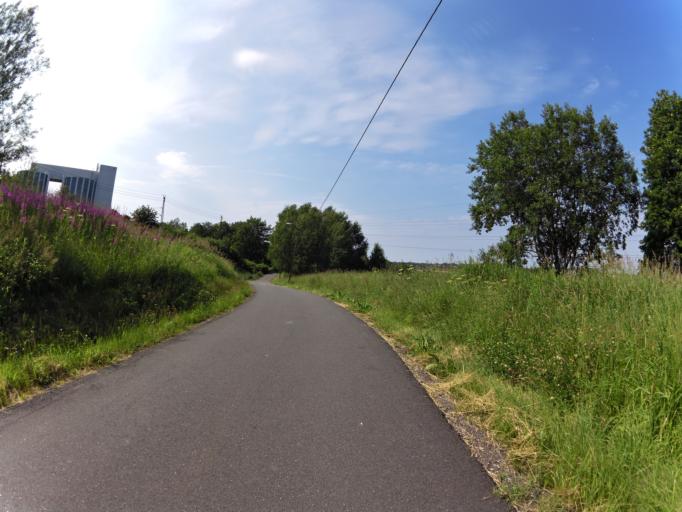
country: NO
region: Ostfold
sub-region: Sarpsborg
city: Sarpsborg
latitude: 59.2792
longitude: 11.1302
